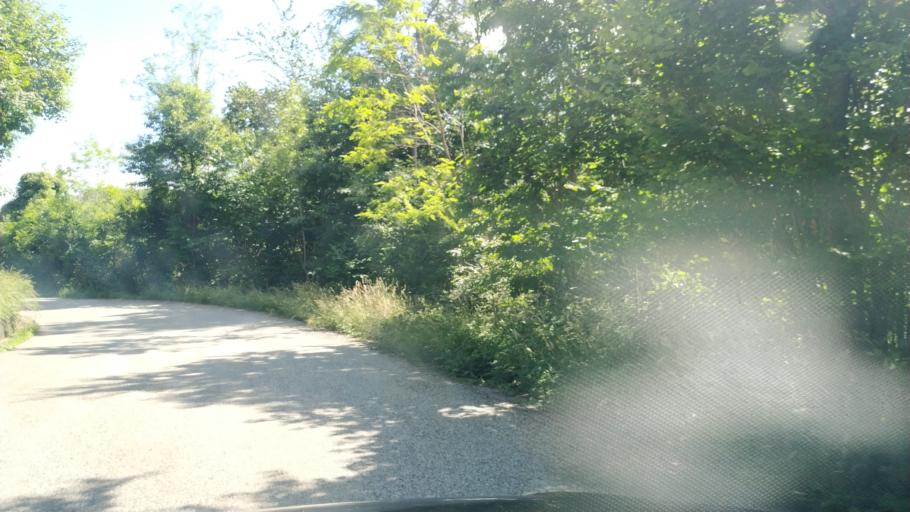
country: IT
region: Piedmont
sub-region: Provincia di Torino
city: Castelnuovo Nigra
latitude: 45.4318
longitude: 7.7002
